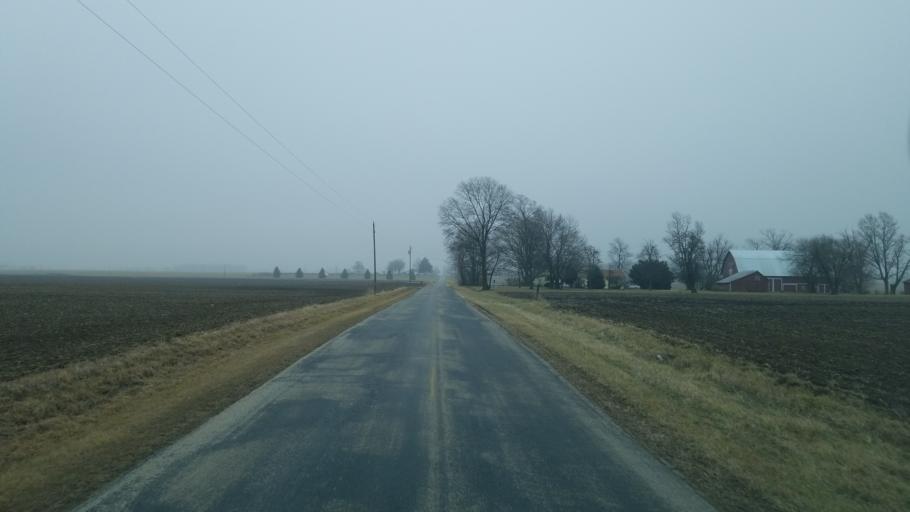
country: US
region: Indiana
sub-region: Adams County
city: Geneva
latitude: 40.6118
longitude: -85.0767
